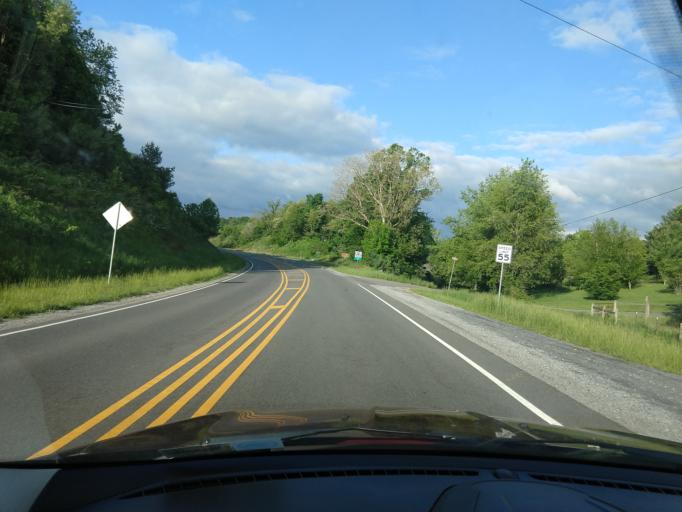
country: US
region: Virginia
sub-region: Wythe County
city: Wytheville
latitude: 36.8936
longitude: -80.9735
